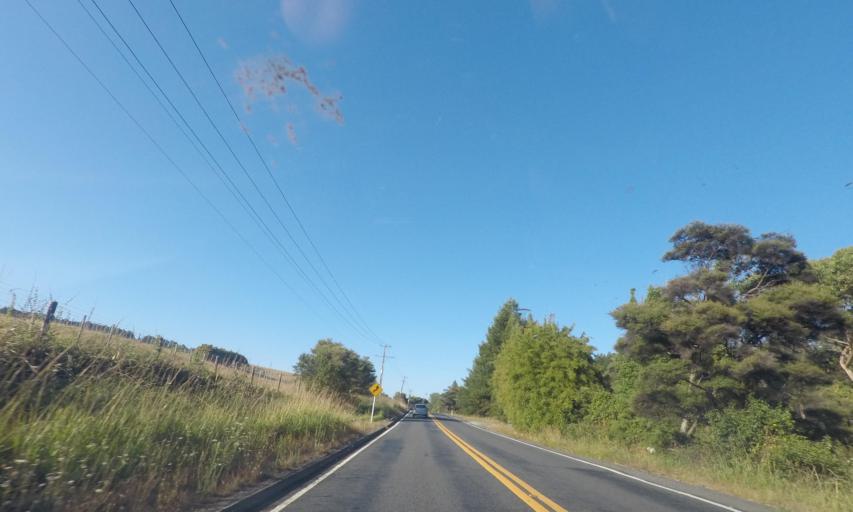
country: NZ
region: Auckland
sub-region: Auckland
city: Muriwai Beach
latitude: -36.7830
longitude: 174.4802
